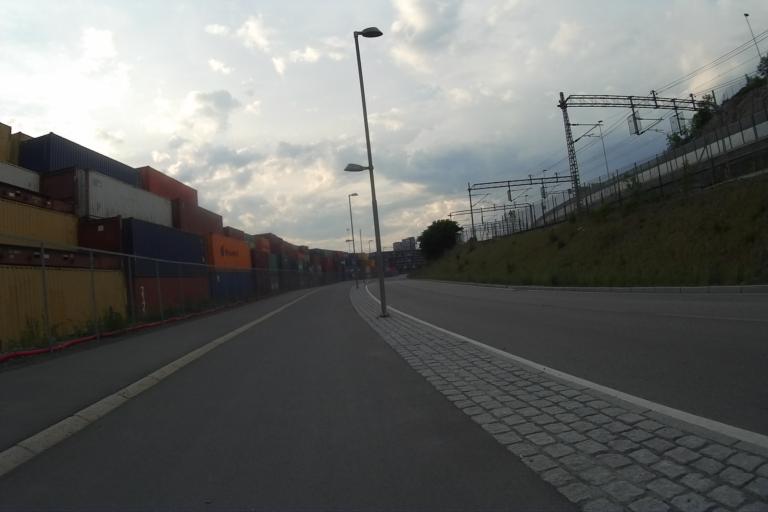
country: NO
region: Oslo
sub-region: Oslo
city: Oslo
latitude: 59.8968
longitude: 10.7553
